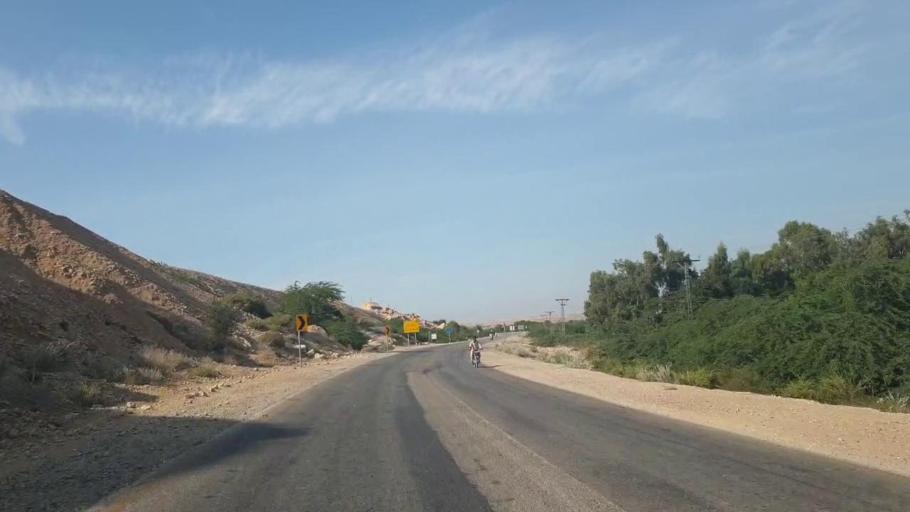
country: PK
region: Sindh
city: Sehwan
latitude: 26.3236
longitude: 67.8842
